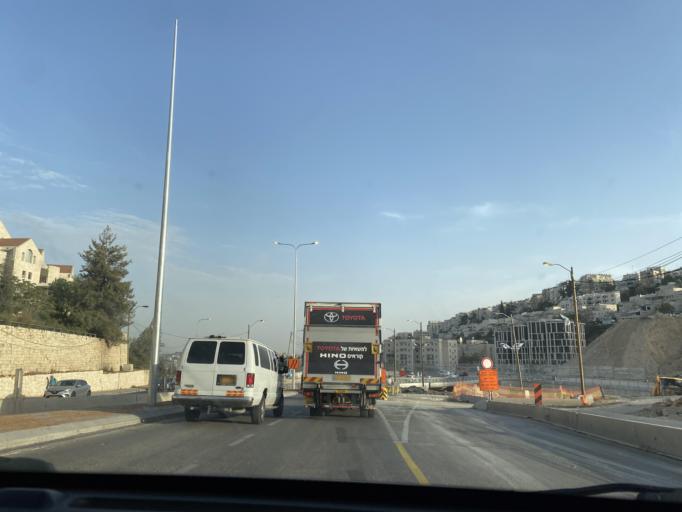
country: IL
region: Jerusalem
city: Jerusalem
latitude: 31.7696
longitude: 35.1898
